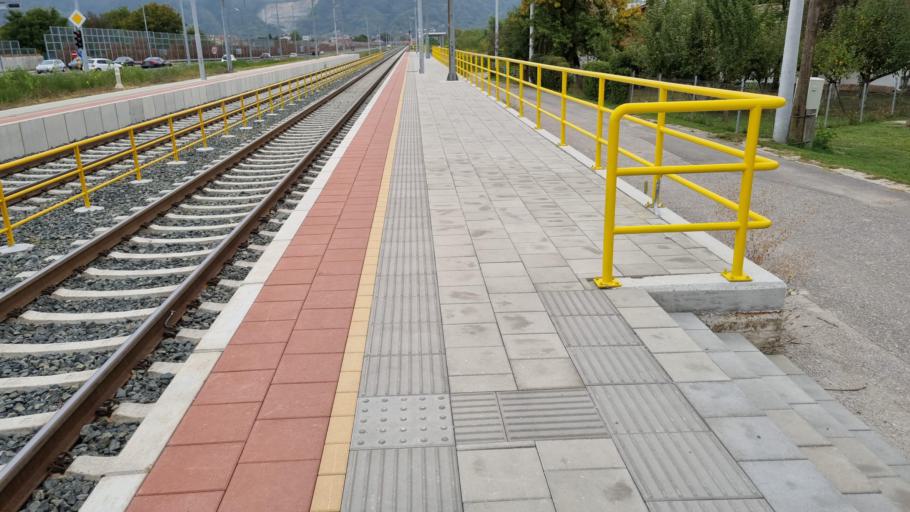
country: HR
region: Zagrebacka
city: Zapresic
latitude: 45.8550
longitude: 15.7948
